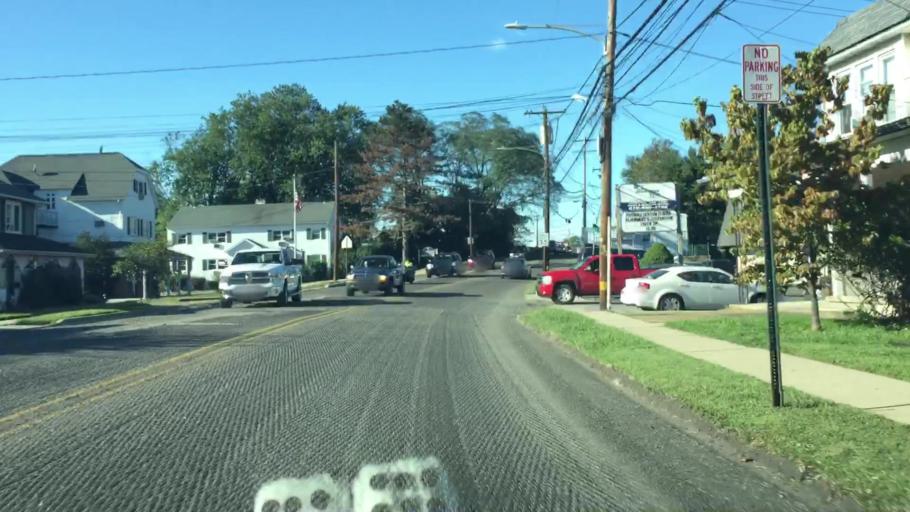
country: US
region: Pennsylvania
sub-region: Delaware County
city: Boothwyn
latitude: 39.8327
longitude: -75.4413
